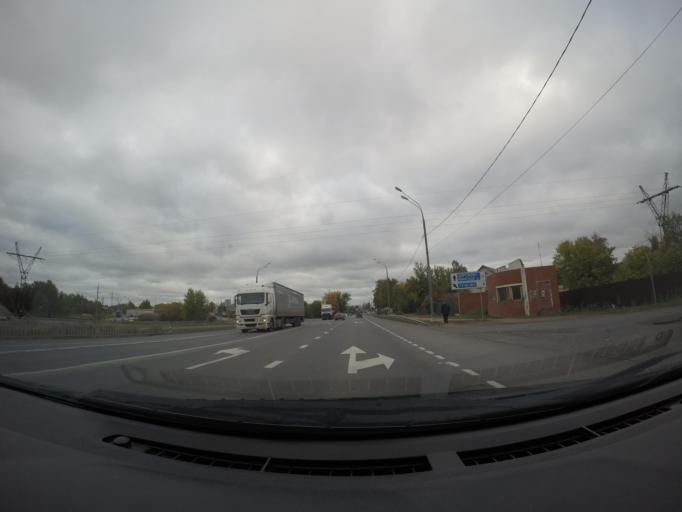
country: RU
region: Moskovskaya
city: Dorokhovo
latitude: 55.6260
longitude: 36.3400
